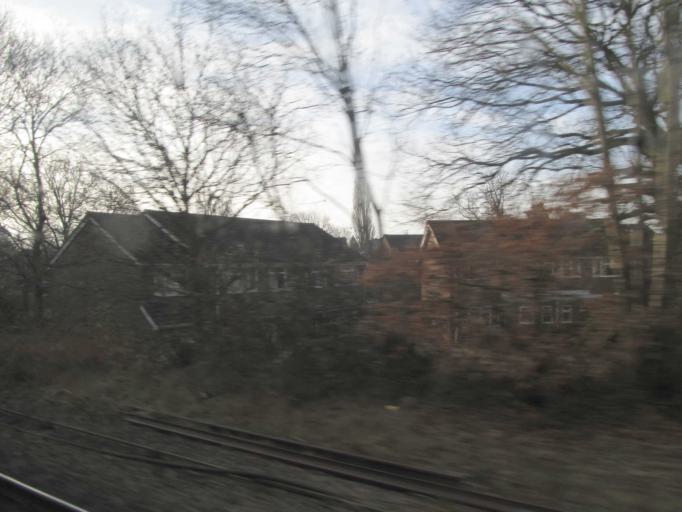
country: GB
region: England
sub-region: Wokingham
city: Earley
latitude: 51.4404
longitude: -0.9139
